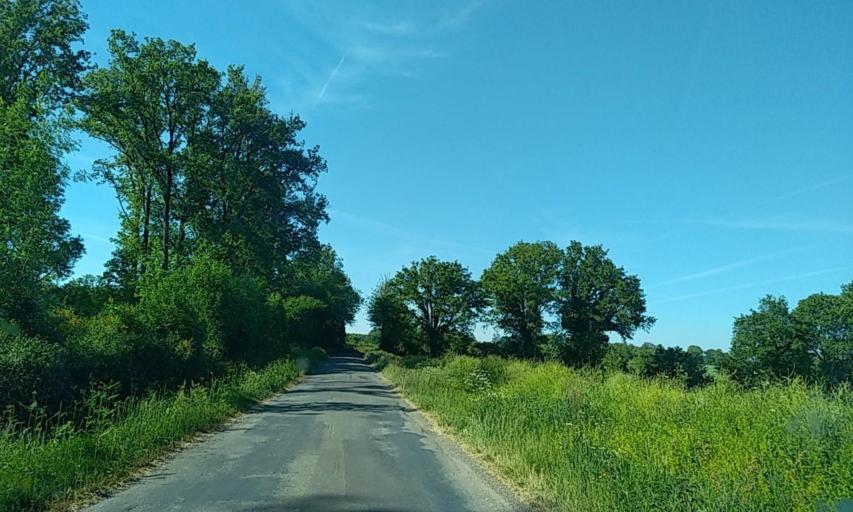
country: FR
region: Poitou-Charentes
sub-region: Departement des Deux-Sevres
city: Boisme
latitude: 46.7813
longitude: -0.4272
